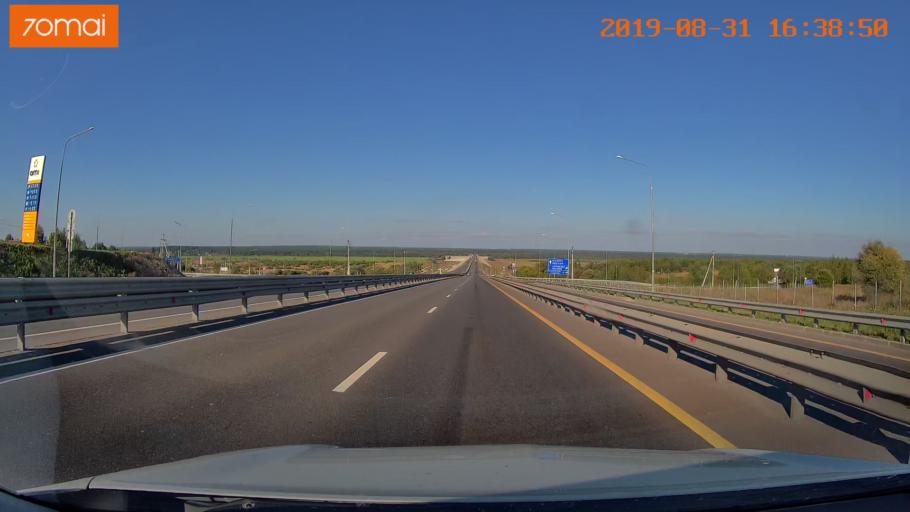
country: RU
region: Kaluga
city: Kurovskoye
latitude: 54.5437
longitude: 36.0127
